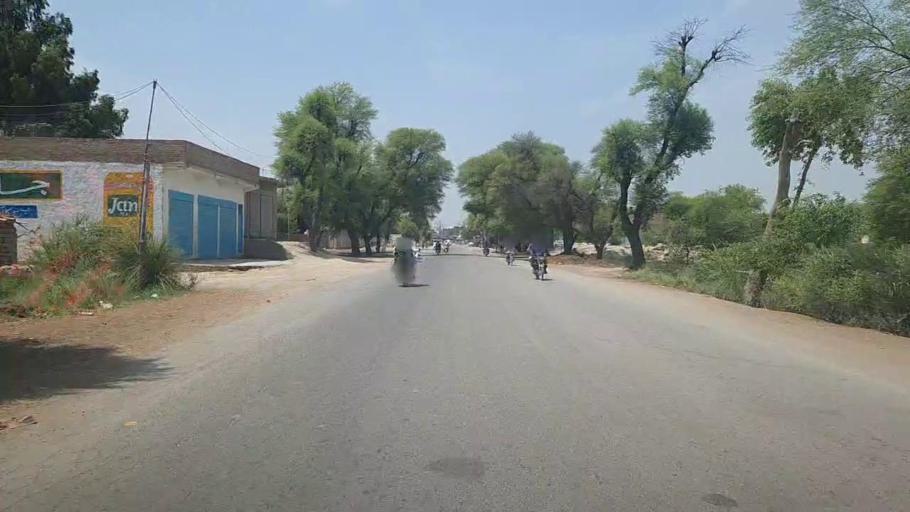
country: PK
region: Sindh
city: Ubauro
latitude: 28.3154
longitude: 69.7971
